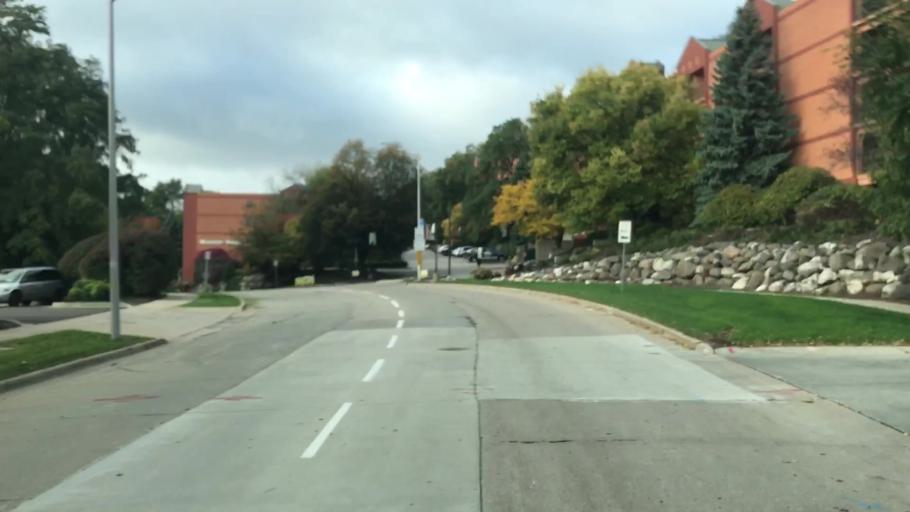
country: US
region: Wisconsin
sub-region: Waukesha County
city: Waukesha
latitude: 43.0115
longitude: -88.2380
